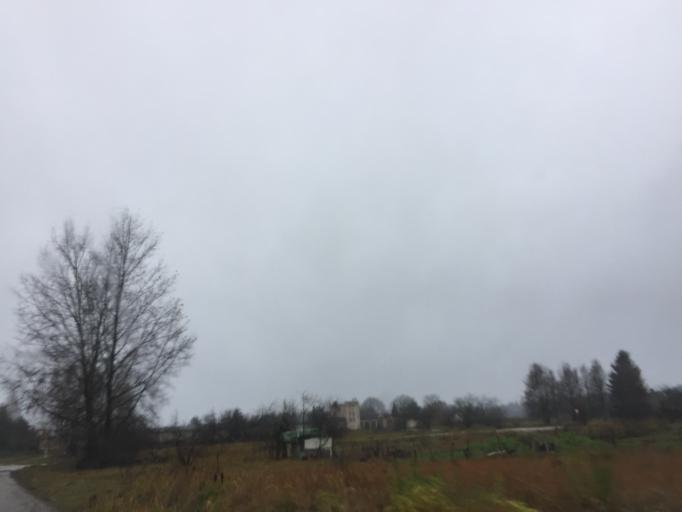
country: LV
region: Jekabpils Rajons
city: Jekabpils
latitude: 56.4896
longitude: 25.8552
